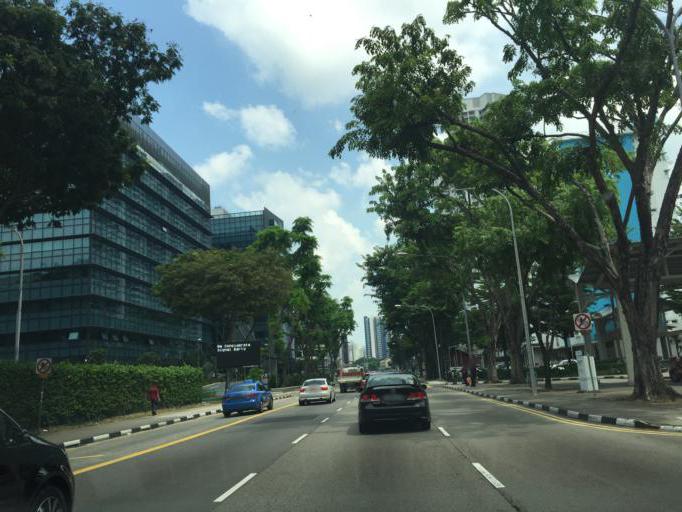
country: SG
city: Singapore
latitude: 1.3182
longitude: 103.8636
